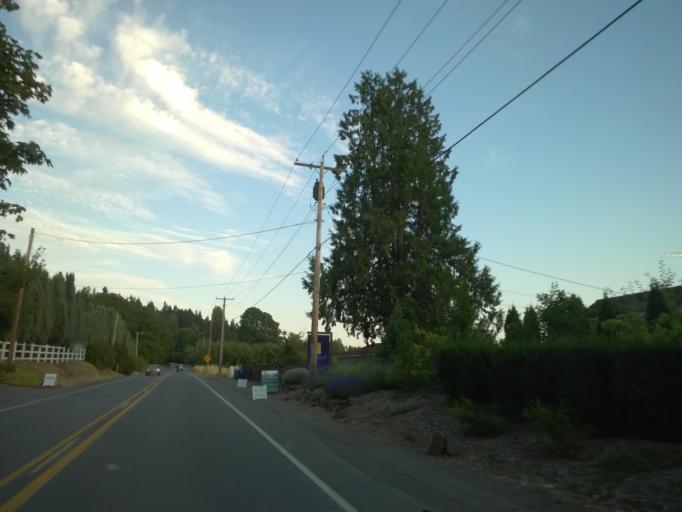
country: US
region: Washington
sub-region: King County
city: Woodinville
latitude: 47.7273
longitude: -122.1372
